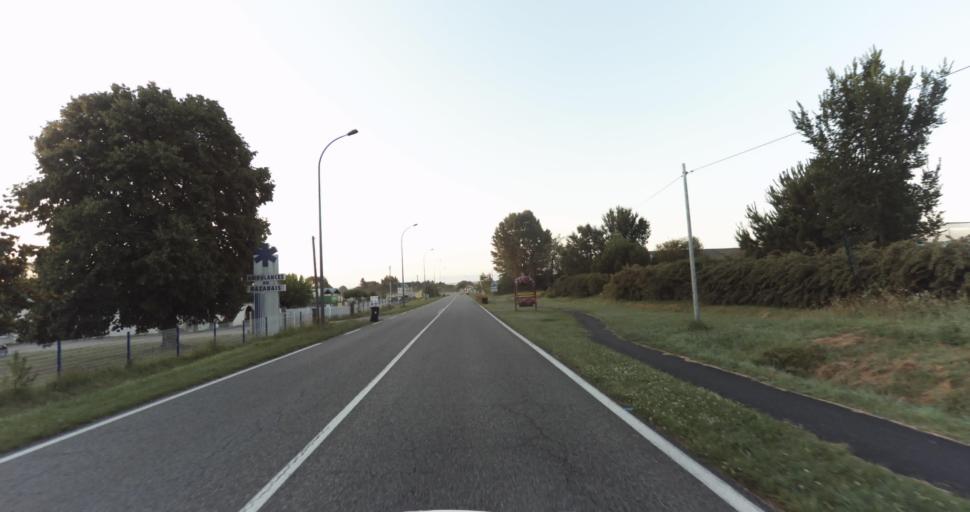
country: FR
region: Aquitaine
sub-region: Departement de la Gironde
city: Bazas
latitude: 44.4402
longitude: -0.2309
